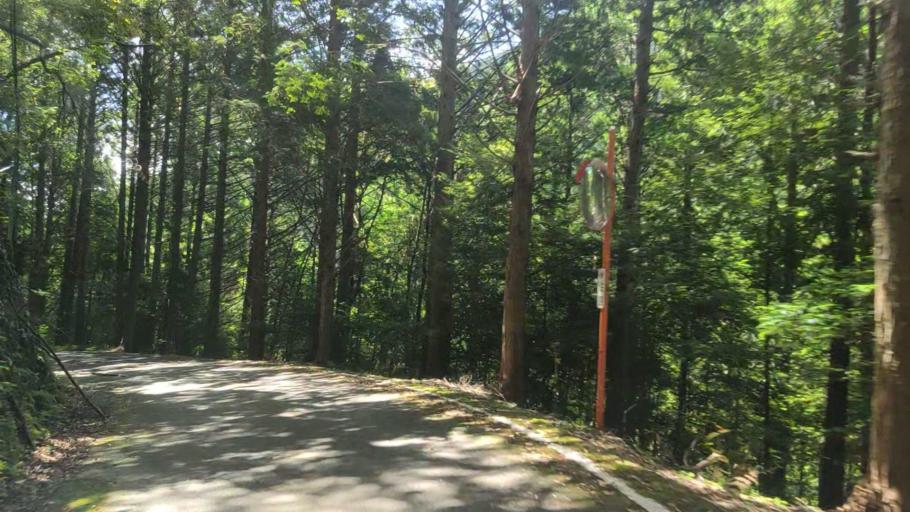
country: JP
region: Wakayama
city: Shingu
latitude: 33.9073
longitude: 135.8658
